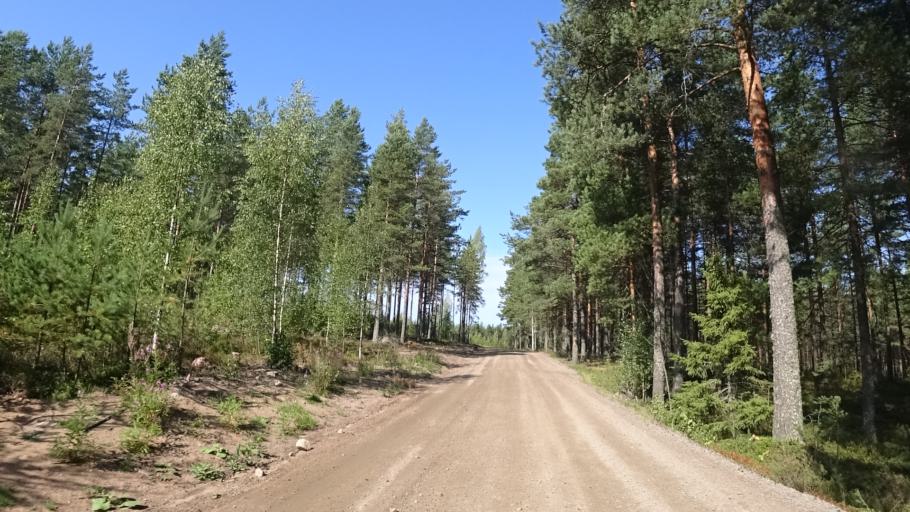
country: FI
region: Kymenlaakso
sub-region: Kotka-Hamina
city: Hamina
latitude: 60.5459
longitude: 27.2171
